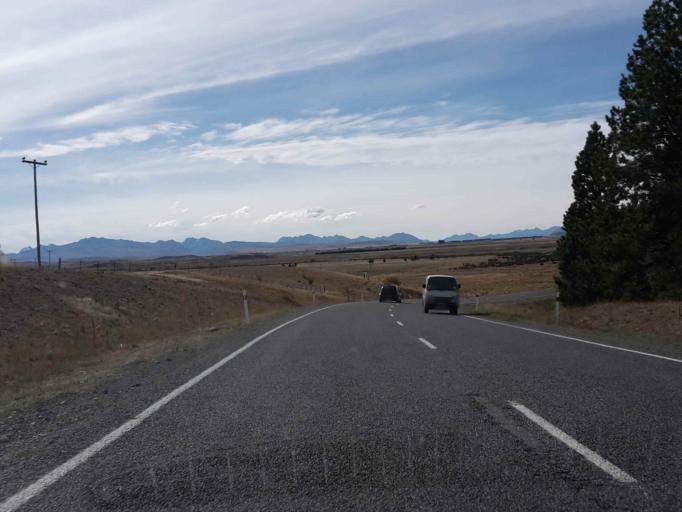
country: NZ
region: Canterbury
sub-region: Timaru District
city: Pleasant Point
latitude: -44.1776
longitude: 170.3199
